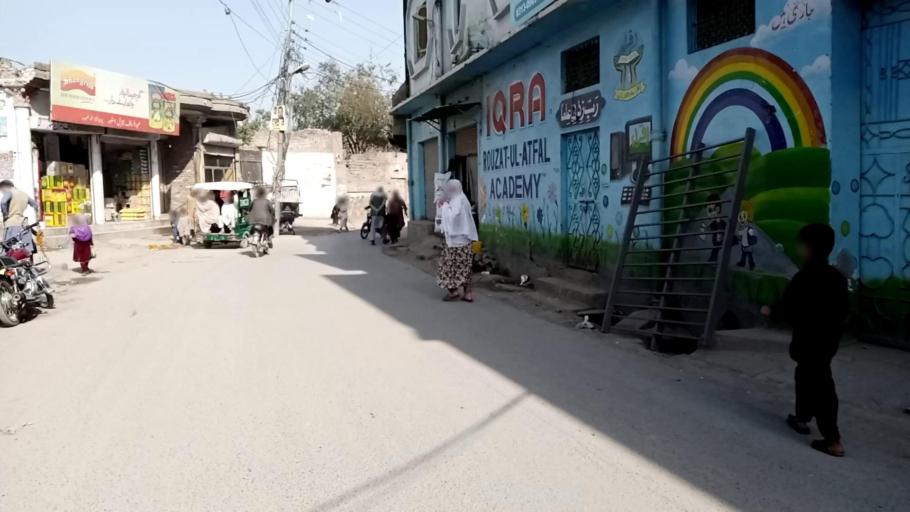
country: PK
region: Khyber Pakhtunkhwa
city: Peshawar
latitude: 33.9970
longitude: 71.5783
